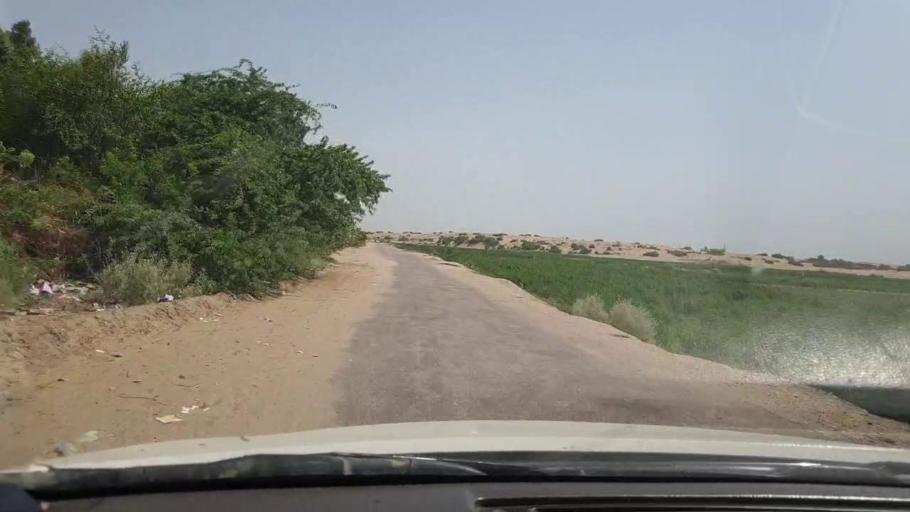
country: PK
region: Sindh
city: Rohri
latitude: 27.4999
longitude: 69.0426
